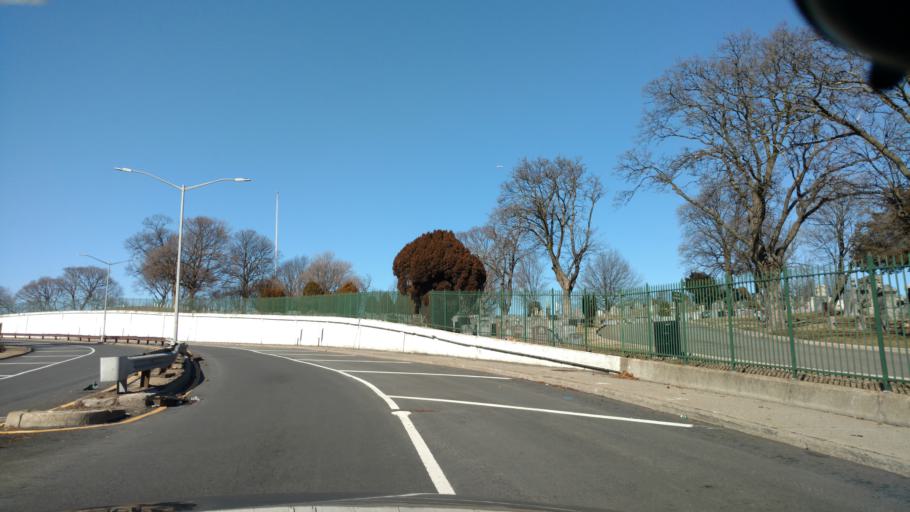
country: US
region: New York
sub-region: Kings County
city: East New York
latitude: 40.6908
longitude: -73.8777
